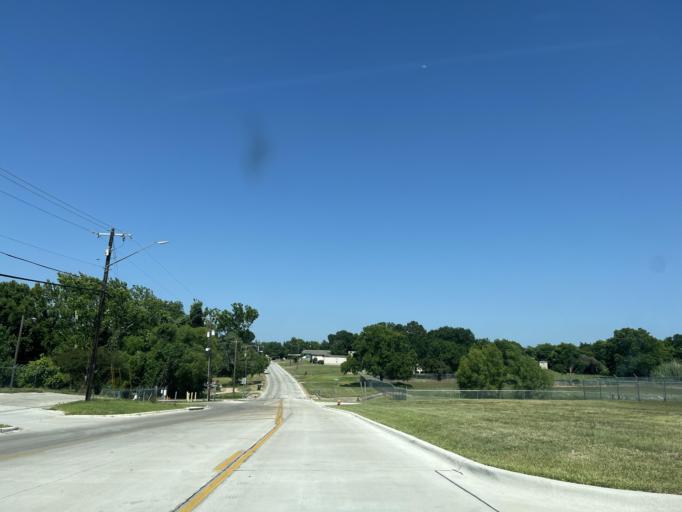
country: US
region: Texas
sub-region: Washington County
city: Brenham
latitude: 30.1701
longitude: -96.3780
